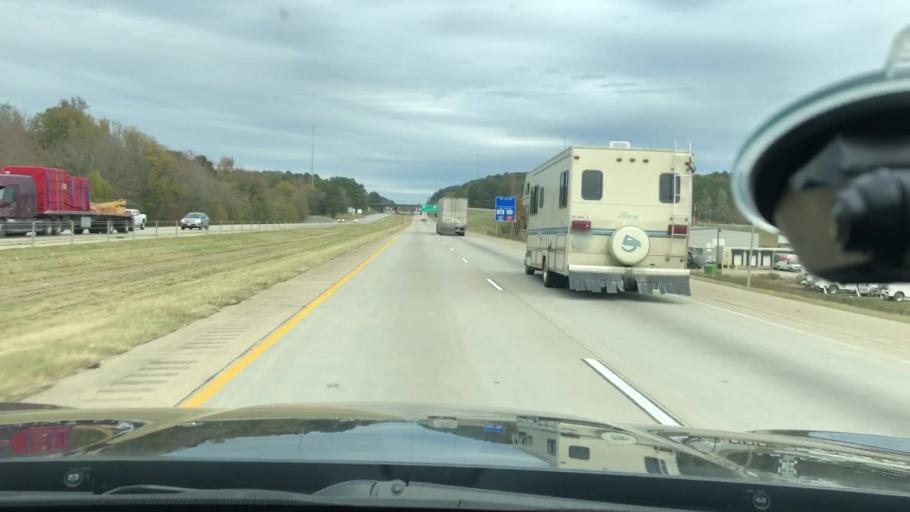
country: US
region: Arkansas
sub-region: Hot Spring County
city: Malvern
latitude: 34.3935
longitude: -92.8336
